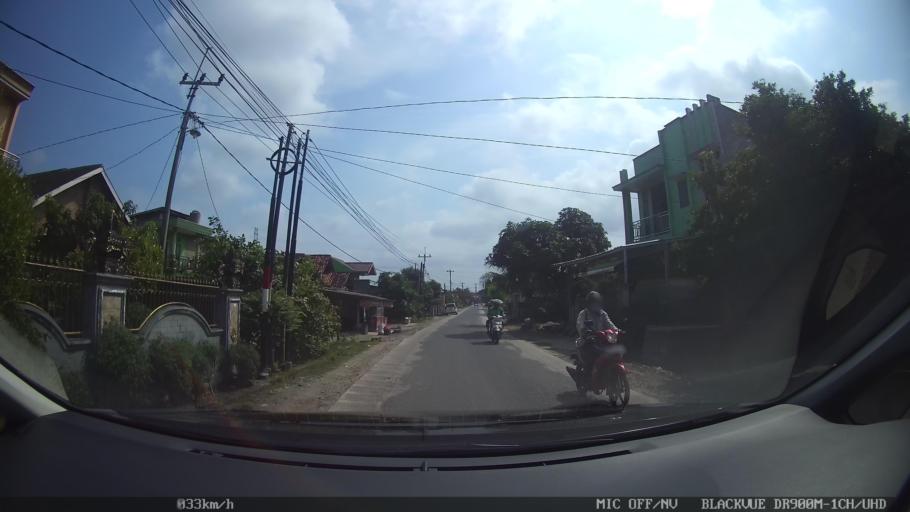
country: ID
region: Lampung
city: Kedaton
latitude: -5.3451
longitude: 105.2678
